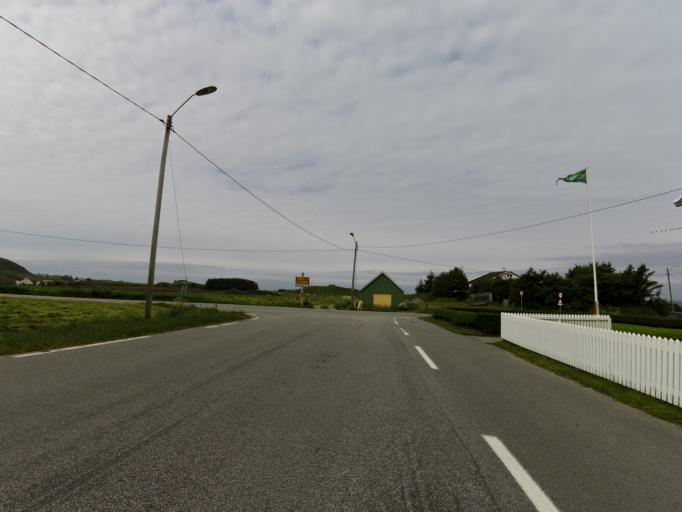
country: NO
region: Rogaland
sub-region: Sola
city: Tananger
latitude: 58.8663
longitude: 5.5687
